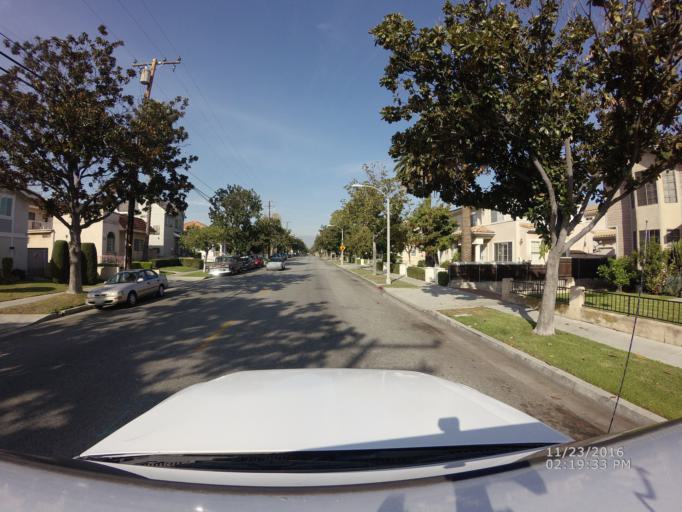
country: US
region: California
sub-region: Los Angeles County
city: Alhambra
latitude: 34.0931
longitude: -118.1420
